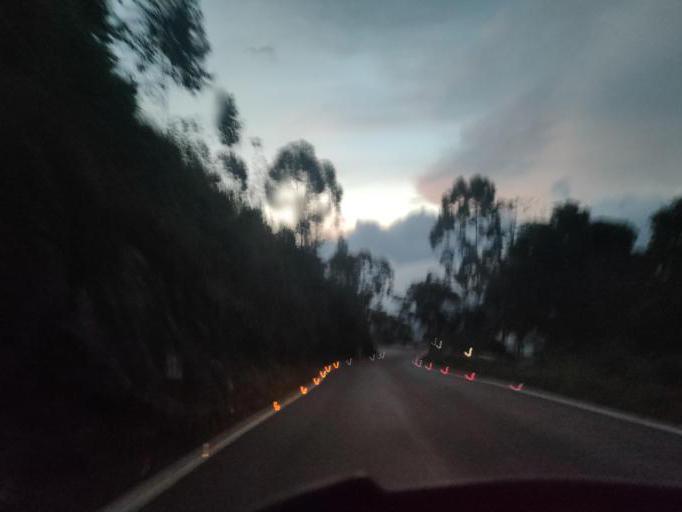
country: IN
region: Tamil Nadu
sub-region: Dindigul
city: Kodaikanal
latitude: 10.2816
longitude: 77.5344
